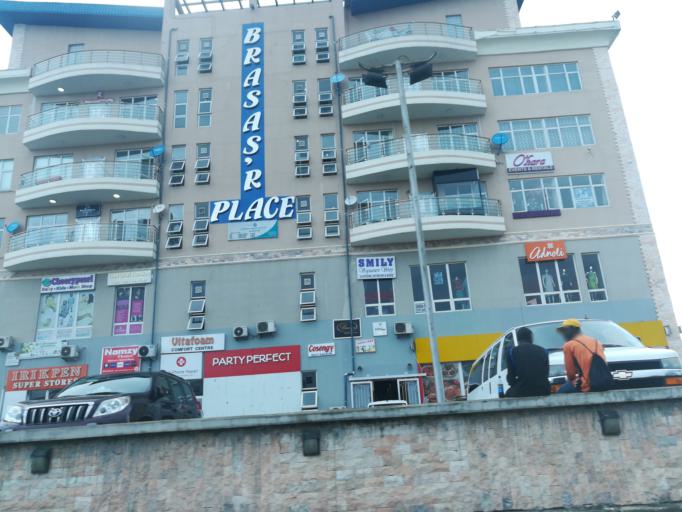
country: NG
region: Lagos
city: Ikoyi
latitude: 6.4474
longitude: 3.4724
